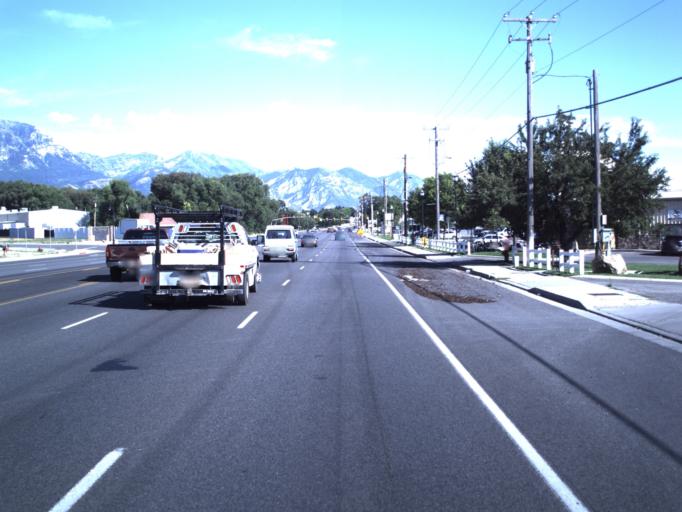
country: US
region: Utah
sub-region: Utah County
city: Lindon
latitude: 40.3473
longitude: -111.7263
